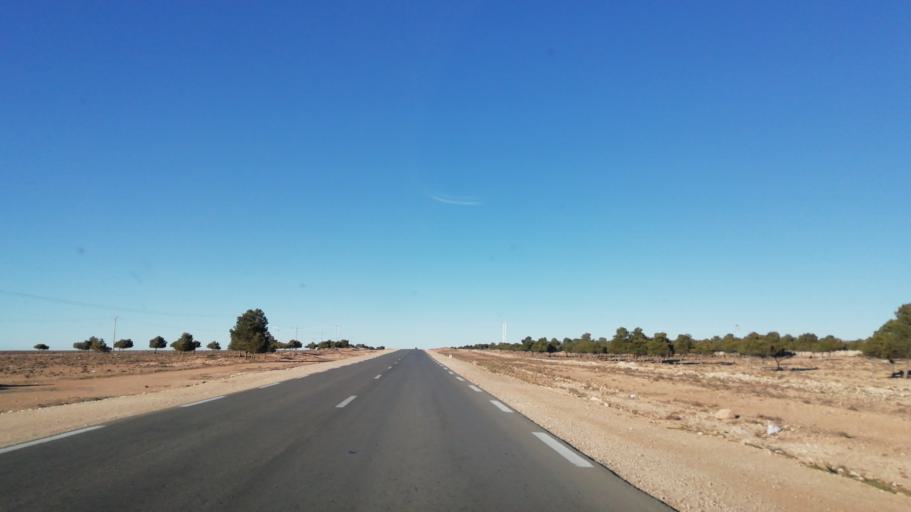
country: DZ
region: Tlemcen
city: Sebdou
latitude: 34.2411
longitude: -1.2568
